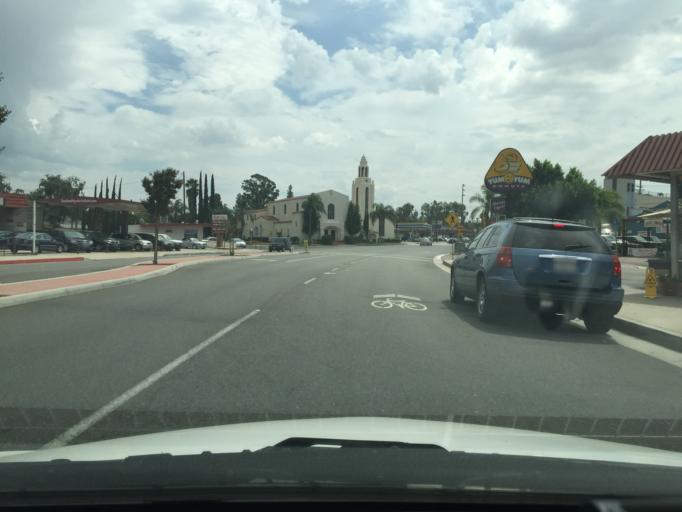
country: US
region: California
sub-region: San Bernardino County
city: Redlands
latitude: 34.0568
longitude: -117.1772
